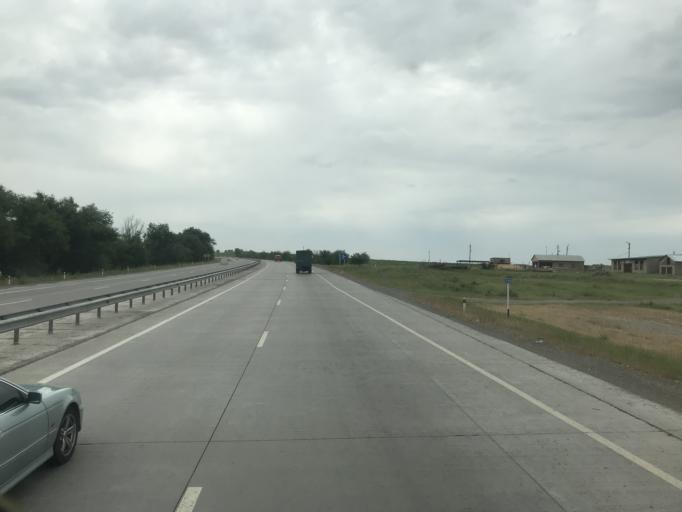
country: KZ
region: Ongtustik Qazaqstan
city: Shymkent
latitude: 42.2072
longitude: 69.5142
